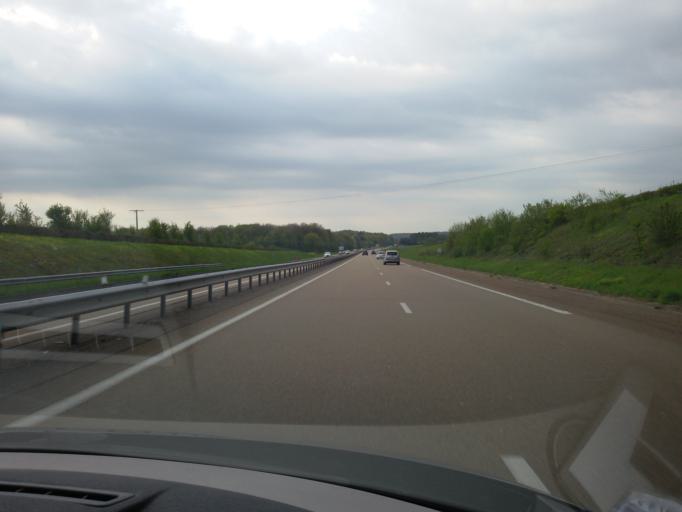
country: FR
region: Champagne-Ardenne
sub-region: Departement de la Haute-Marne
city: Chamarandes-Choignes
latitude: 47.9789
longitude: 5.1344
